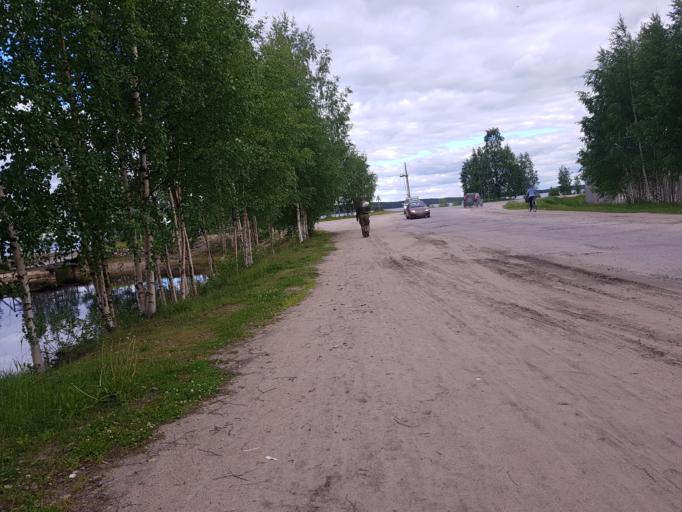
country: RU
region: Republic of Karelia
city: Kalevala
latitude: 65.1959
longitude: 31.1830
